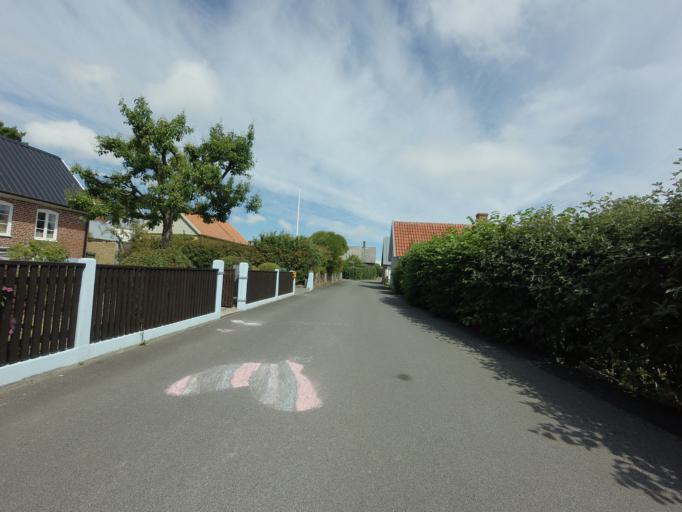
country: SE
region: Skane
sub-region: Simrishamns Kommun
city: Simrishamn
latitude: 55.5189
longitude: 14.3464
